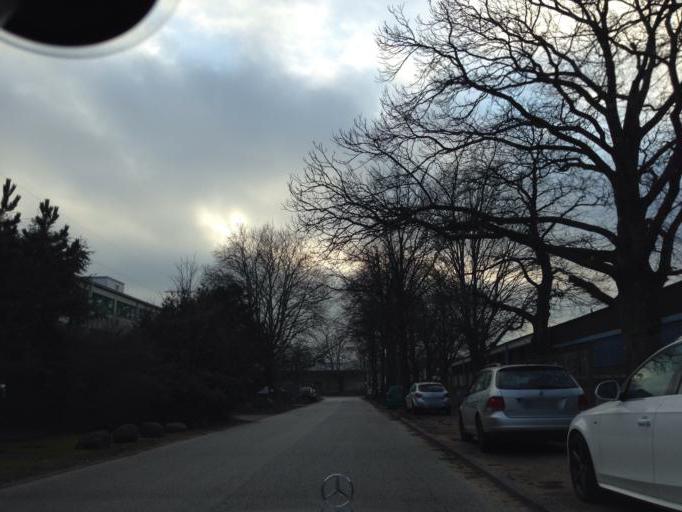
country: DE
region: Hamburg
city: Wandsbek
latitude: 53.5781
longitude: 10.1120
